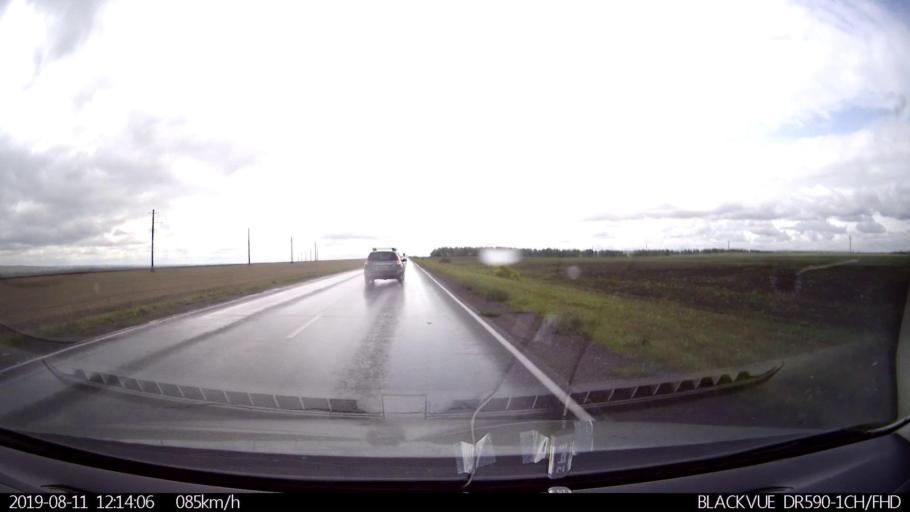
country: RU
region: Ulyanovsk
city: Ignatovka
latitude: 53.9554
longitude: 47.9844
